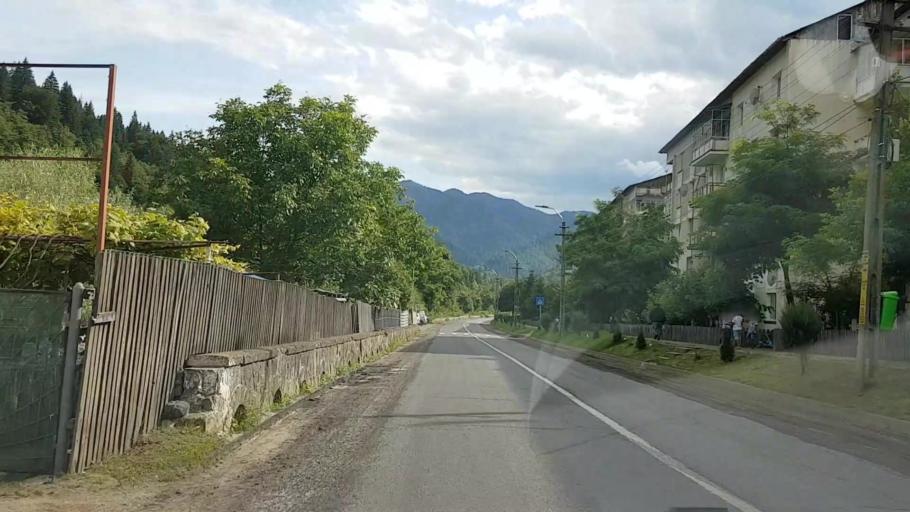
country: RO
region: Neamt
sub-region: Comuna Bicaz
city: Dodeni
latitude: 46.9269
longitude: 26.0944
